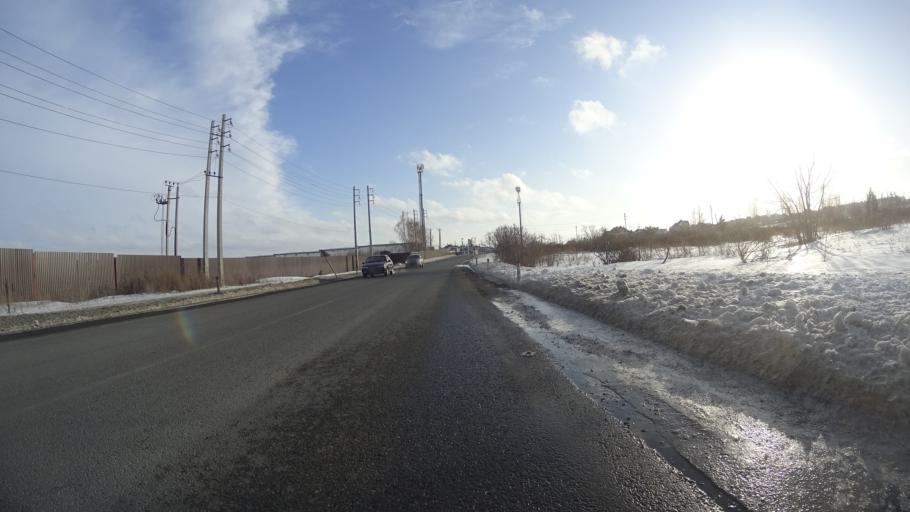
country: RU
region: Chelyabinsk
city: Sargazy
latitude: 55.1198
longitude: 61.2867
